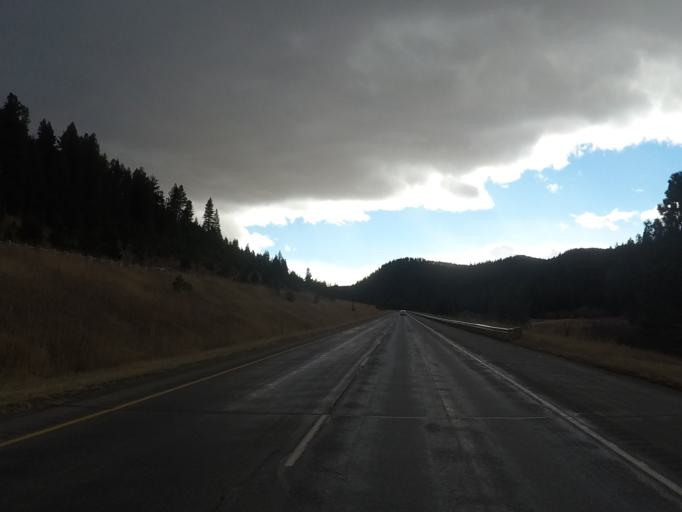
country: US
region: Montana
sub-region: Jefferson County
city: Clancy
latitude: 46.3639
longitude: -112.0392
